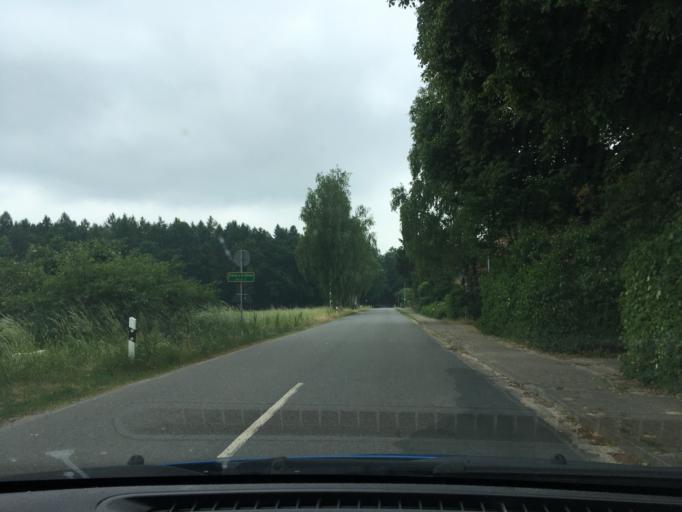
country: DE
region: Lower Saxony
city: Zernien
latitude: 53.0889
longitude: 10.8848
